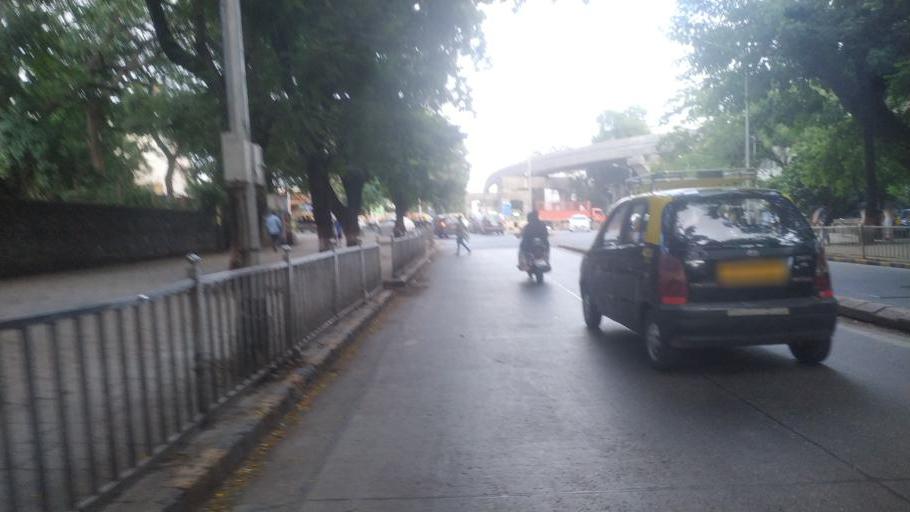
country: IN
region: Maharashtra
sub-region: Mumbai Suburban
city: Mumbai
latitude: 19.0193
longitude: 72.8553
